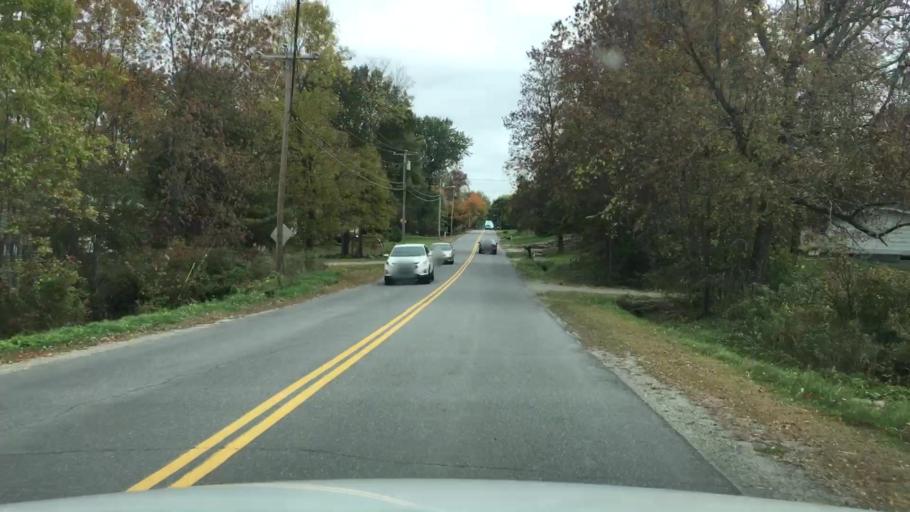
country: US
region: Maine
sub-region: Kennebec County
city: Waterville
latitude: 44.5664
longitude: -69.6766
